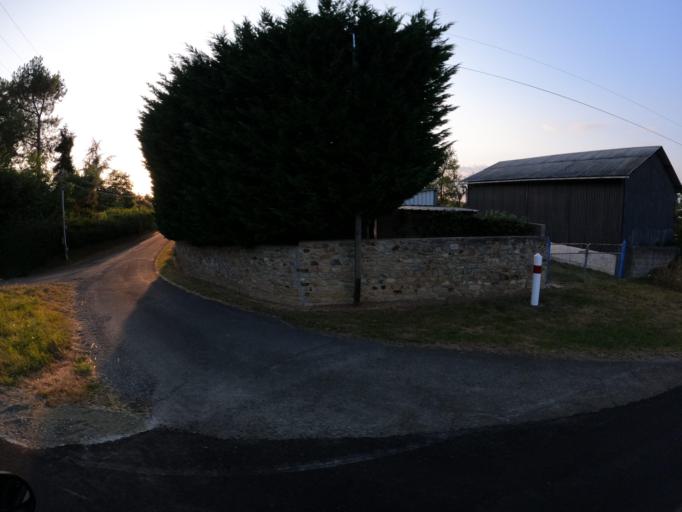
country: FR
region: Pays de la Loire
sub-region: Departement de la Sarthe
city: Auvers-le-Hamon
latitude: 47.8726
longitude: -0.4008
